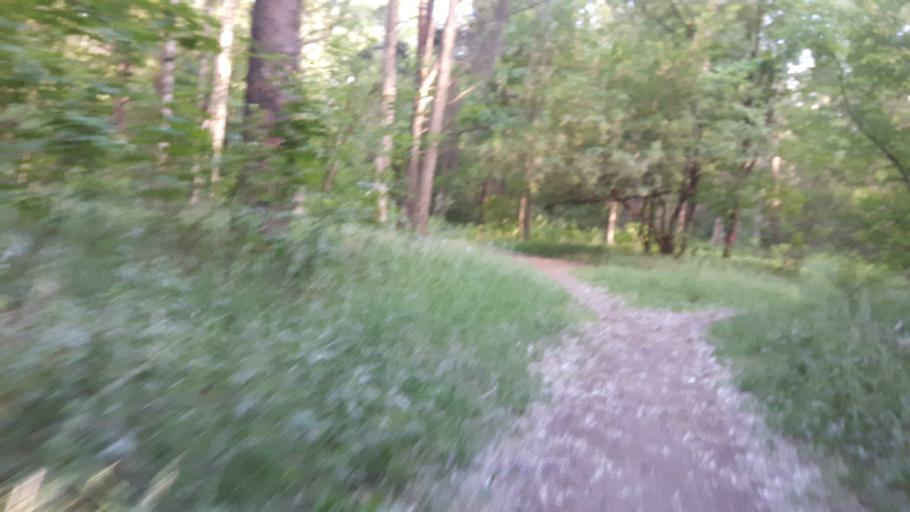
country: LV
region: Riga
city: Jaunciems
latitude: 57.0151
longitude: 24.1336
